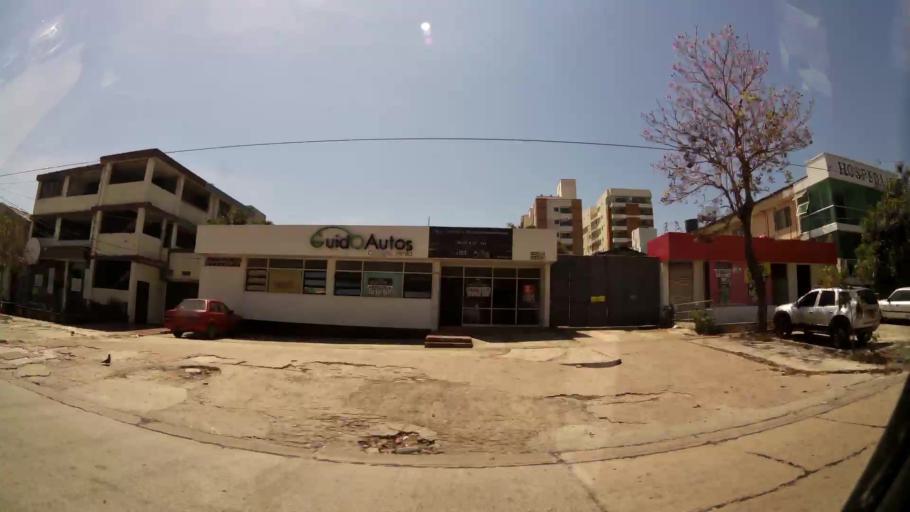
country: CO
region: Atlantico
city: Barranquilla
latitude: 10.9971
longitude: -74.8170
